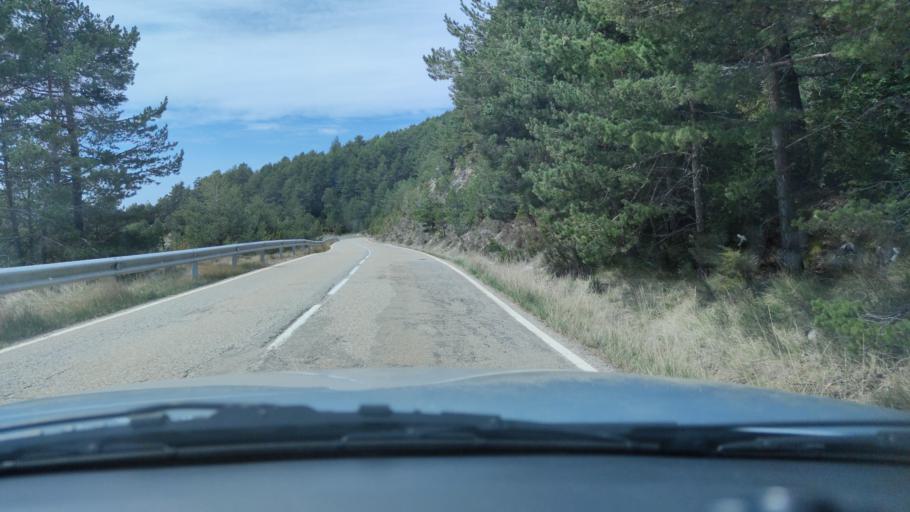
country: ES
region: Catalonia
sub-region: Provincia de Lleida
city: Olius
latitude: 42.1467
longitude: 1.5547
